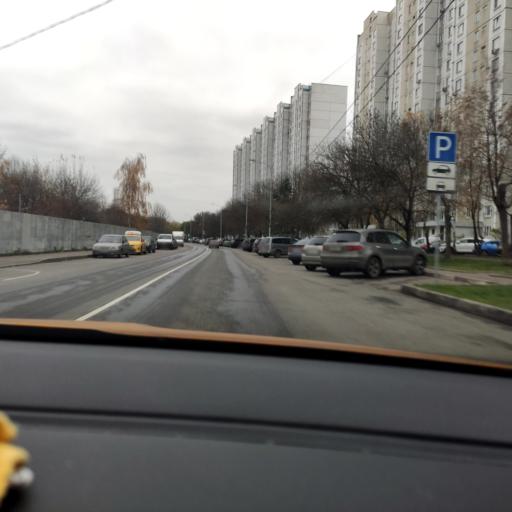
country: RU
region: Moscow
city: Zyablikovo
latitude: 55.6101
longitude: 37.7554
